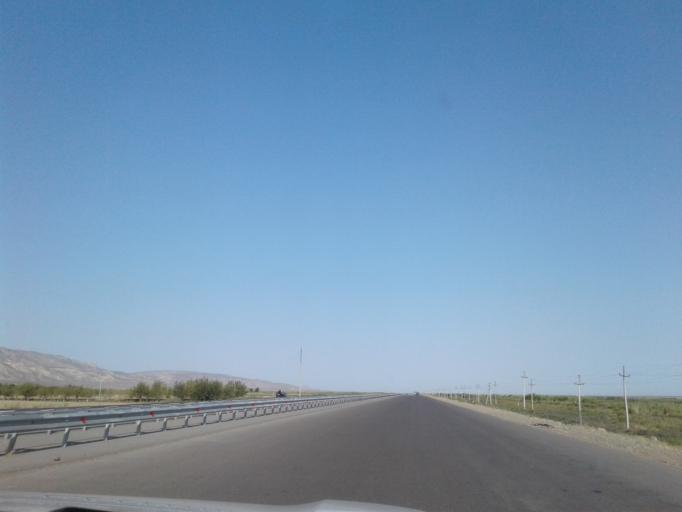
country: TM
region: Balkan
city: Serdar
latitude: 38.8729
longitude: 56.5690
